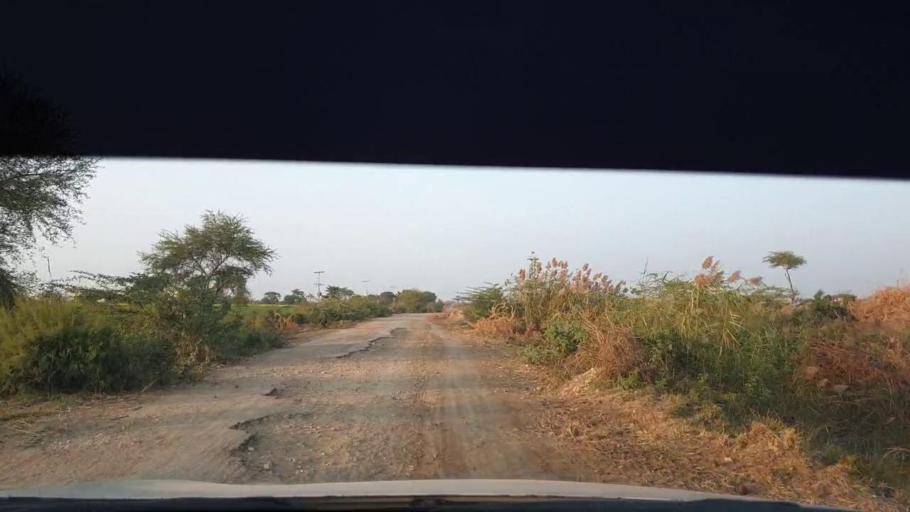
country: PK
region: Sindh
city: Berani
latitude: 25.7526
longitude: 68.9817
